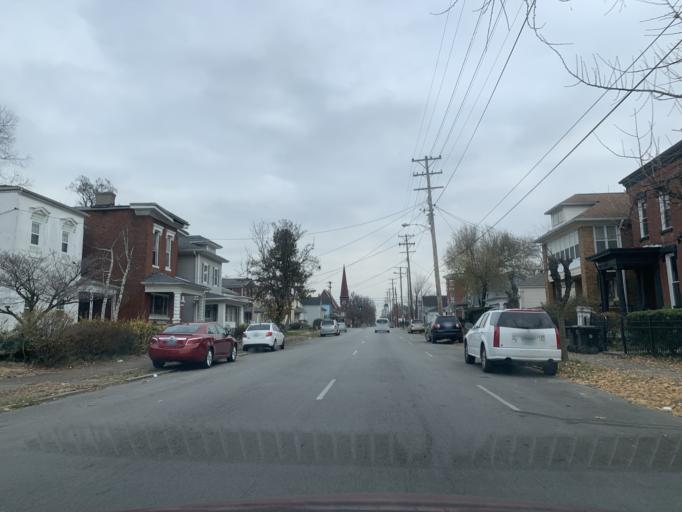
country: US
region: Kentucky
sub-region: Jefferson County
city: Louisville
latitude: 38.2518
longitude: -85.7841
